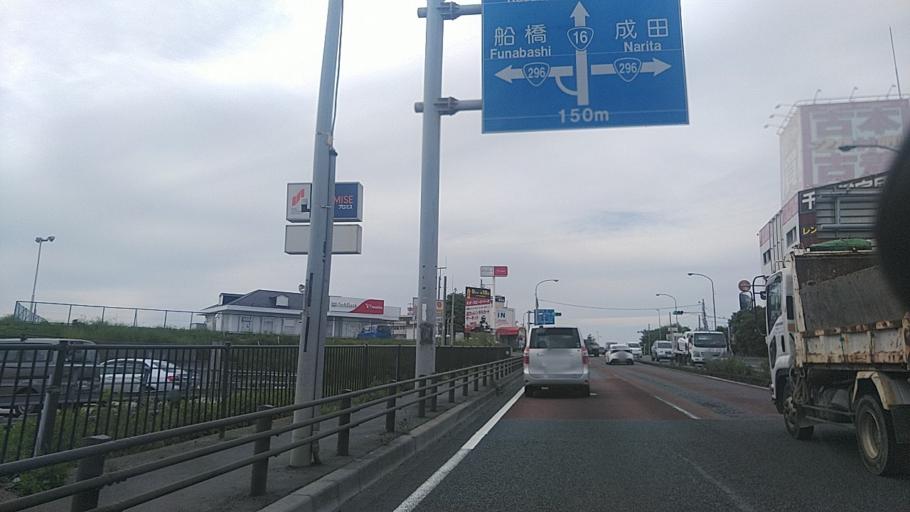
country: JP
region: Chiba
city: Yotsukaido
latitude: 35.7132
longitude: 140.1179
